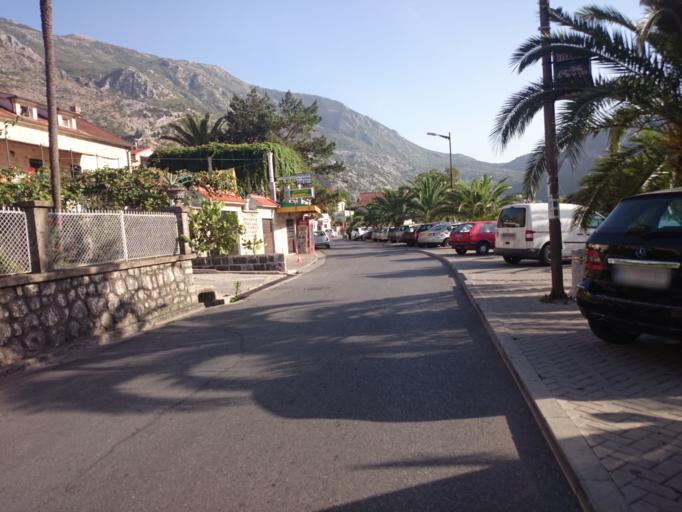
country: ME
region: Kotor
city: Kotor
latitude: 42.4317
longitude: 18.7673
